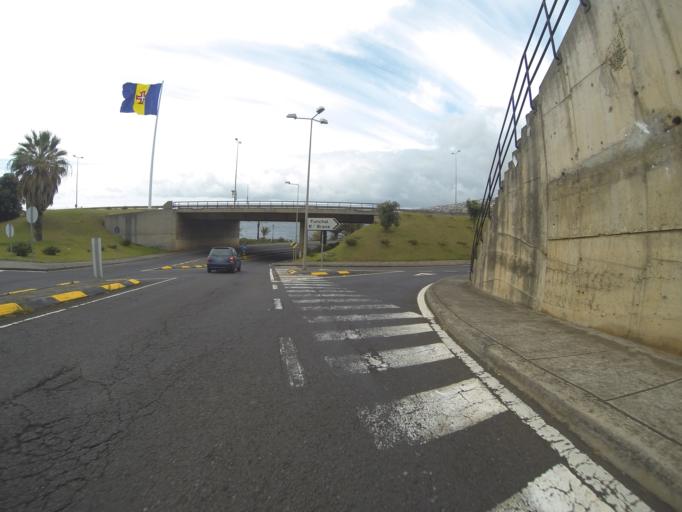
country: PT
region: Madeira
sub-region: Santa Cruz
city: Santa Cruz
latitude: 32.6891
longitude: -16.7858
